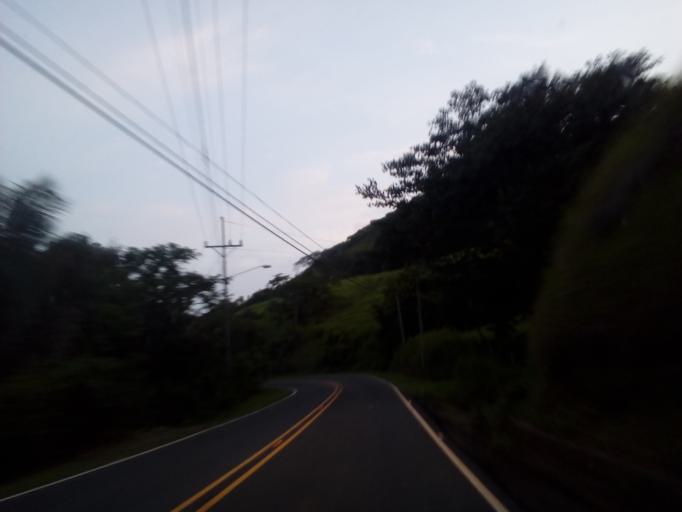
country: CR
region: Guanacaste
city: Hojancha
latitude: 10.0152
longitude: -85.5007
